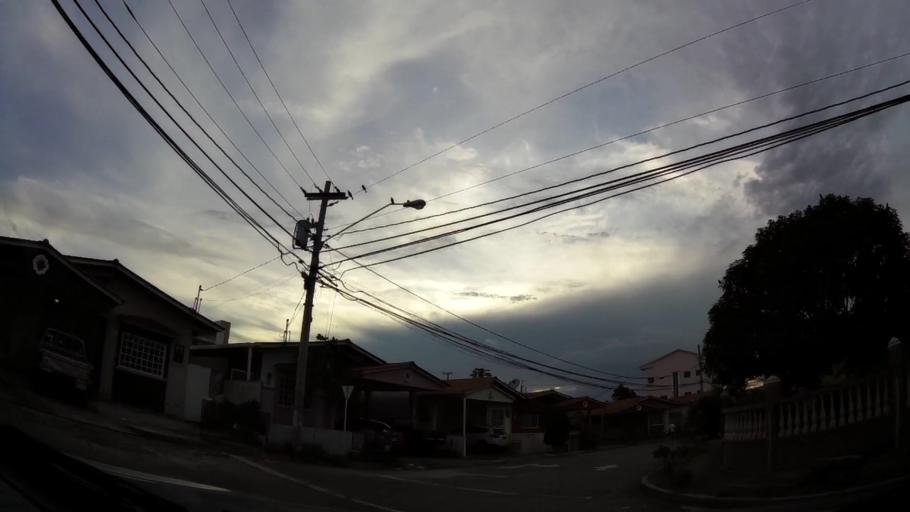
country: PA
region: Panama
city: La Chorrera
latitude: 8.8671
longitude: -79.7664
